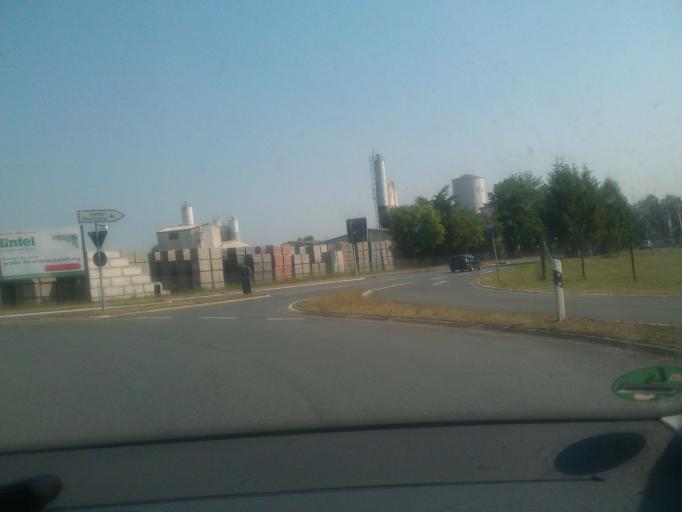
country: DE
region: North Rhine-Westphalia
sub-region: Regierungsbezirk Detmold
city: Lage
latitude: 52.0383
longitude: 8.8289
